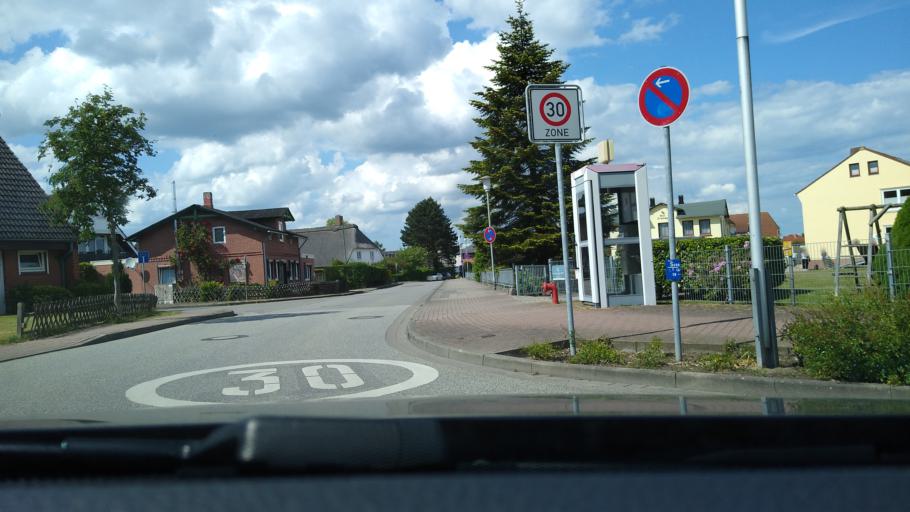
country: DE
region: Schleswig-Holstein
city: Dahme
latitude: 54.2243
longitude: 11.0816
